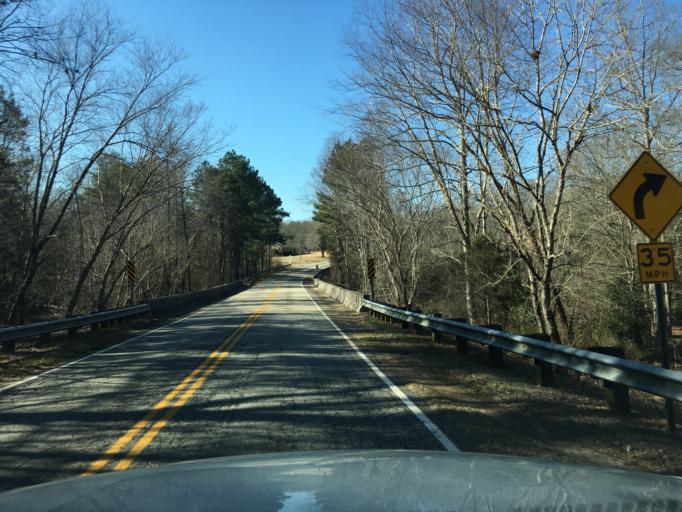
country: US
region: South Carolina
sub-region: Pickens County
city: Pickens
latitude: 34.8595
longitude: -82.7442
